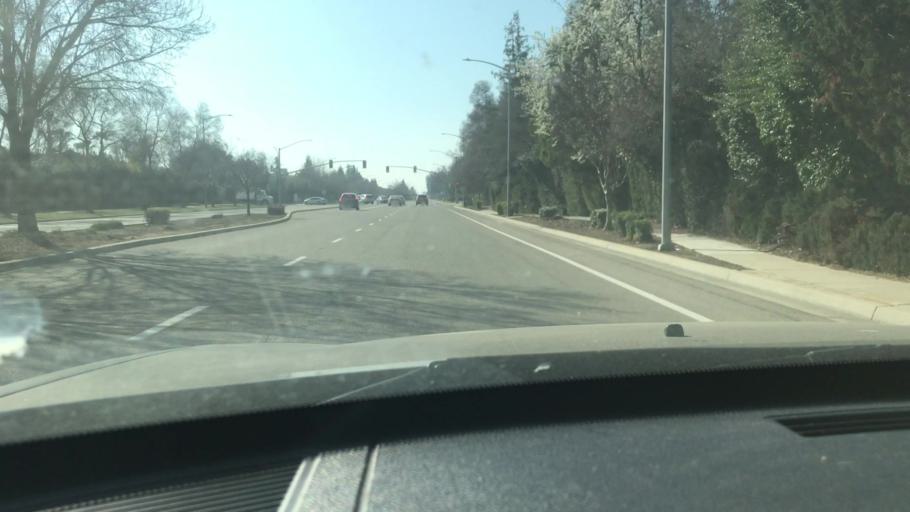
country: US
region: California
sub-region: Fresno County
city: Tarpey Village
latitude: 36.8025
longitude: -119.6641
